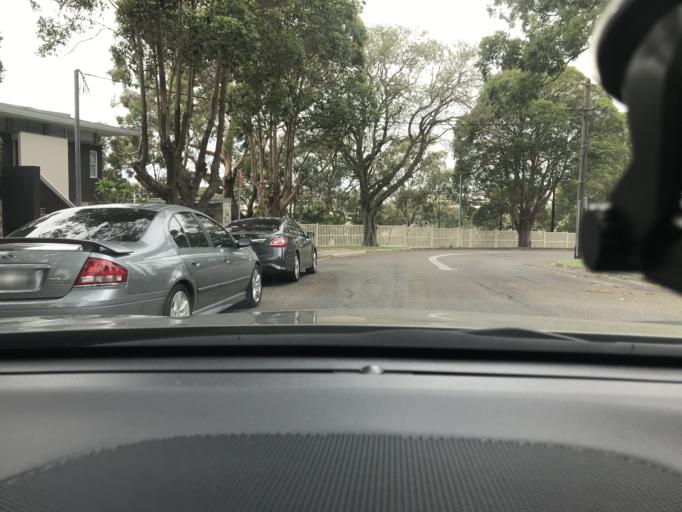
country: AU
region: New South Wales
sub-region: Canada Bay
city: Wareemba
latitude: -33.8478
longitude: 151.1316
